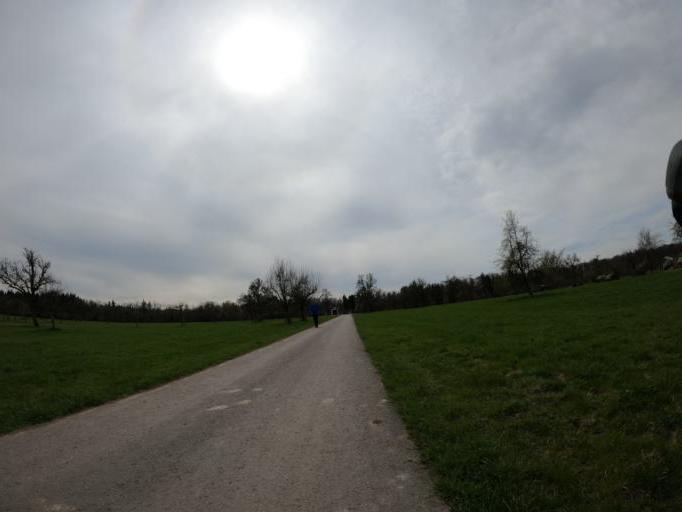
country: DE
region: Baden-Wuerttemberg
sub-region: Regierungsbezirk Stuttgart
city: Waldenbuch
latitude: 48.6186
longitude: 9.1227
